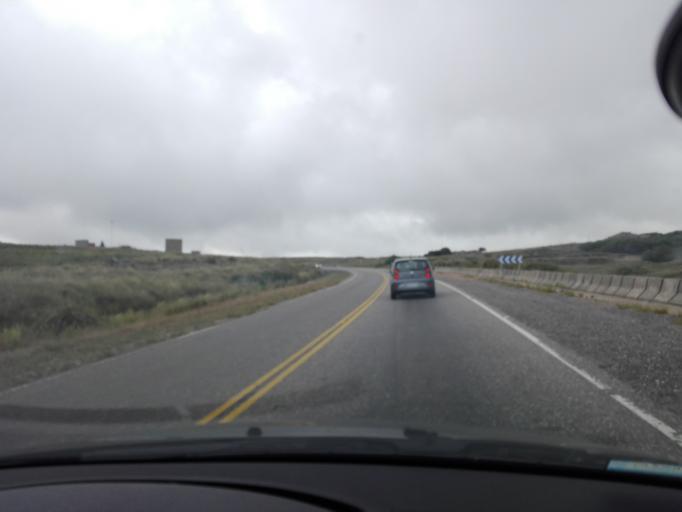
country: AR
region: Cordoba
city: Cuesta Blanca
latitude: -31.6088
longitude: -64.7552
